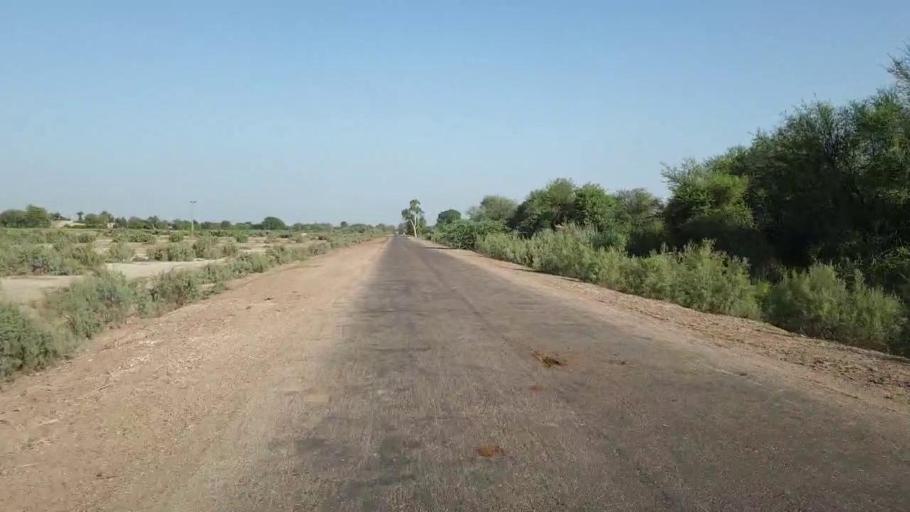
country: PK
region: Sindh
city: Nawabshah
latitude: 26.3852
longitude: 68.4545
